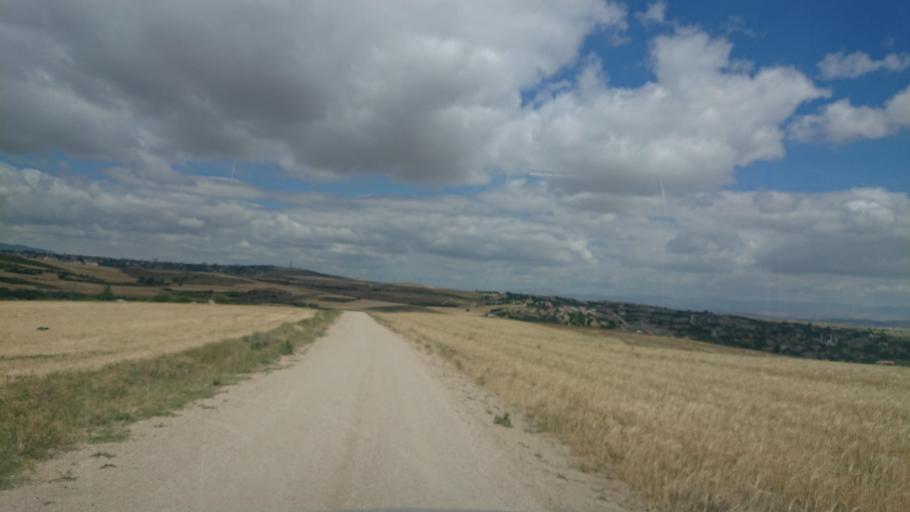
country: TR
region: Aksaray
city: Agacoren
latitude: 38.8557
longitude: 33.9506
